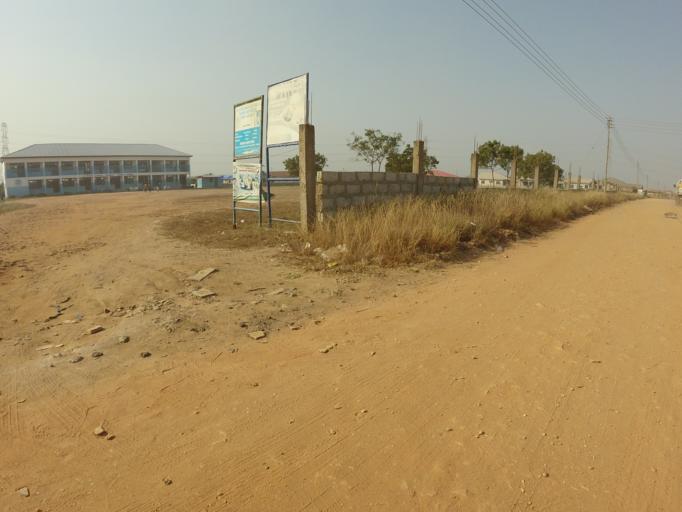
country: GH
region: Greater Accra
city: Tema
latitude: 5.7079
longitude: 0.0577
